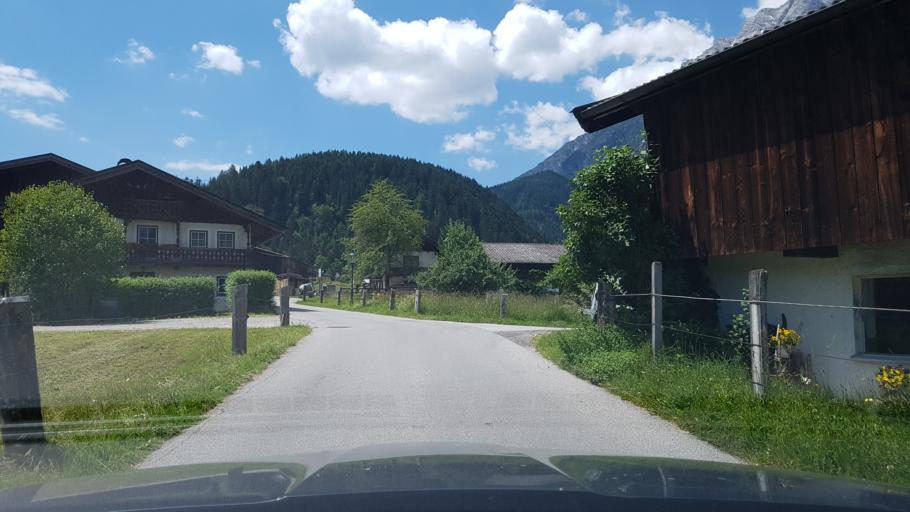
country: AT
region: Salzburg
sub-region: Politischer Bezirk Zell am See
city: Leogang
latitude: 47.4452
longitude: 12.7737
